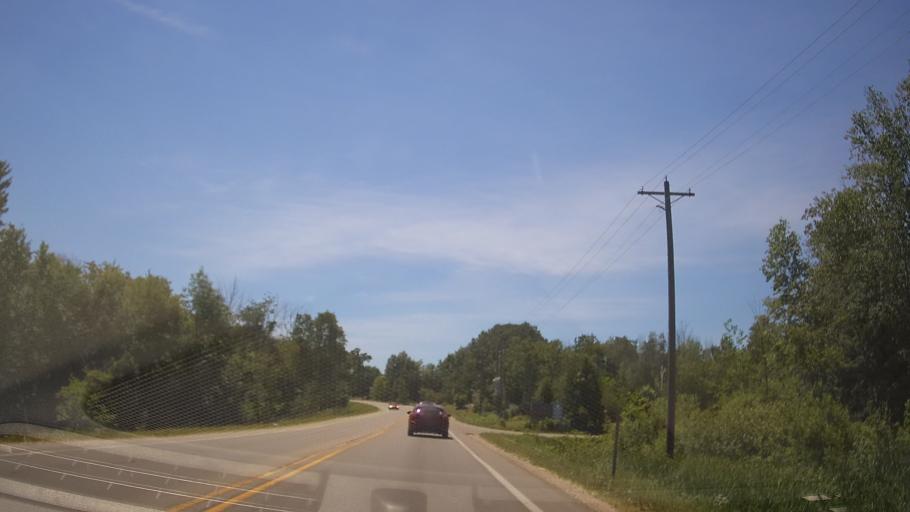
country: US
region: Michigan
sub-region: Grand Traverse County
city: Traverse City
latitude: 44.7330
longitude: -85.6581
